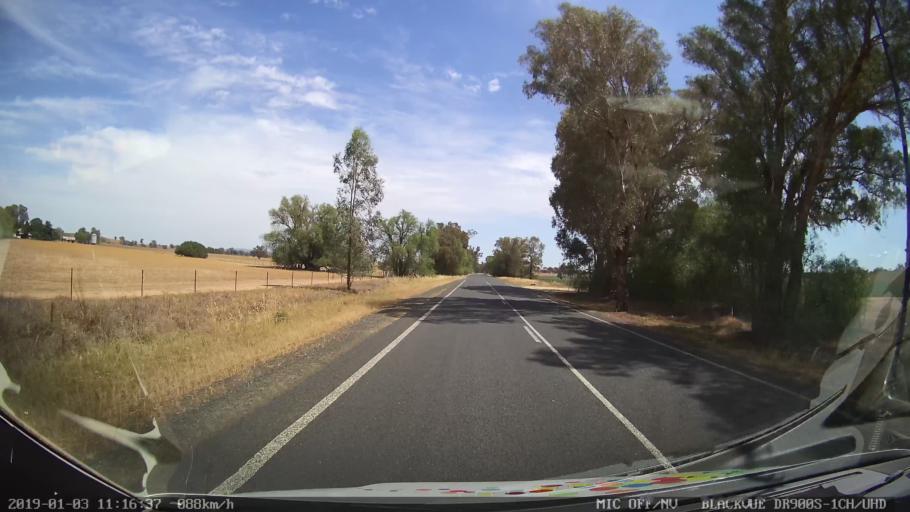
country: AU
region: New South Wales
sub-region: Young
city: Young
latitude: -34.1494
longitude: 148.2692
